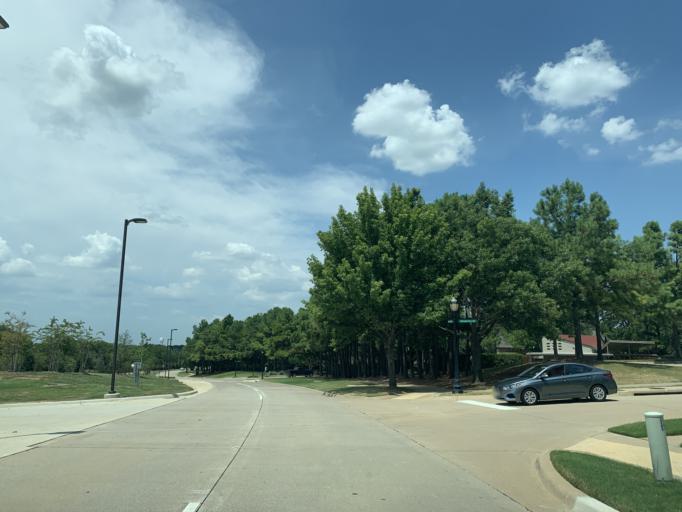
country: US
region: Texas
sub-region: Tarrant County
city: Southlake
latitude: 32.9732
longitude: -97.1547
